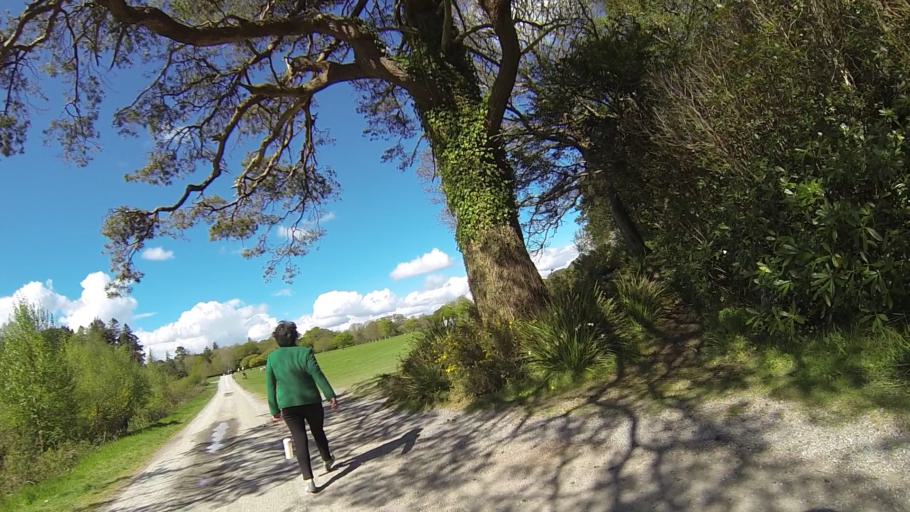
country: IE
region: Munster
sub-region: Ciarrai
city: Cill Airne
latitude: 52.0164
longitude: -9.5067
